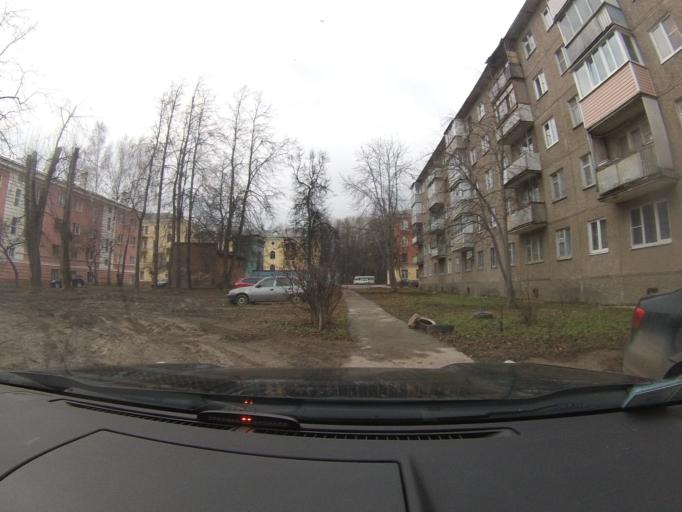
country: RU
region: Moskovskaya
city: Peski
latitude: 55.2521
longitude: 38.7591
